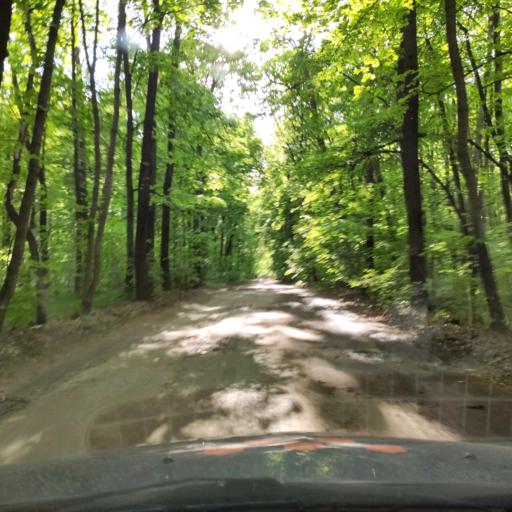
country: RU
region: Voronezj
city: Podgornoye
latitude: 51.7439
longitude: 39.2107
